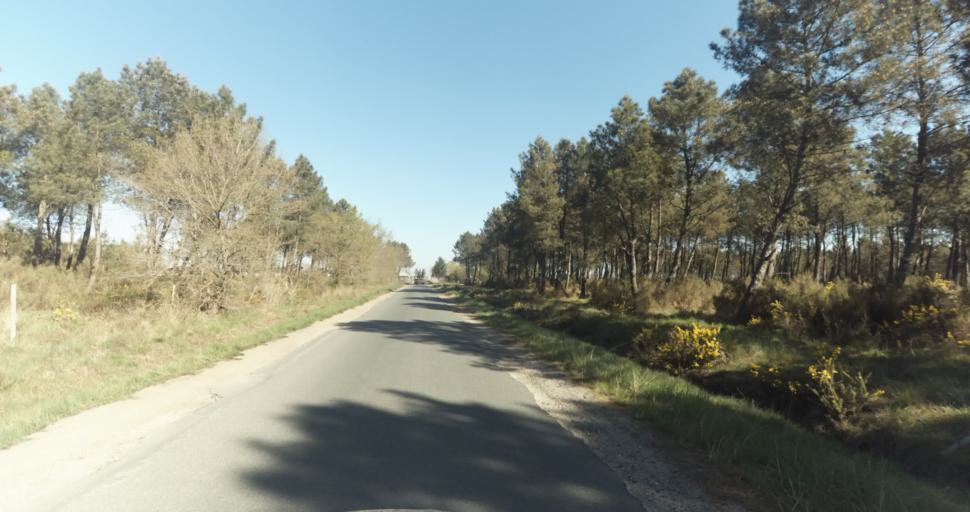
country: FR
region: Aquitaine
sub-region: Departement de la Gironde
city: Marcheprime
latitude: 44.7613
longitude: -0.8528
